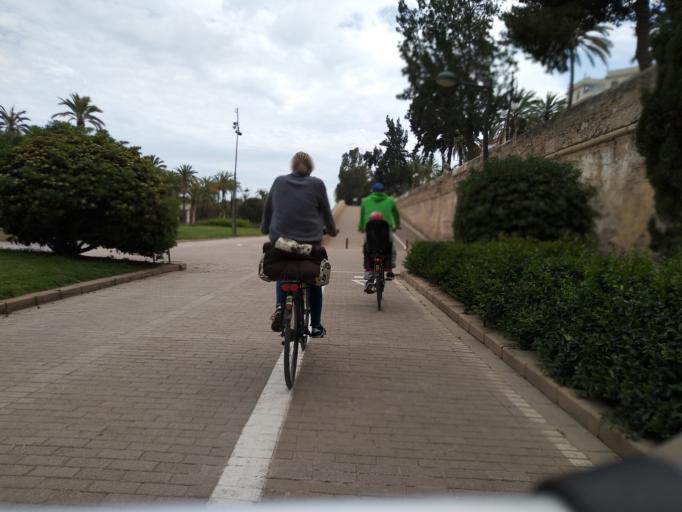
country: ES
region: Valencia
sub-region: Provincia de Valencia
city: Valencia
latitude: 39.4664
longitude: -0.3623
